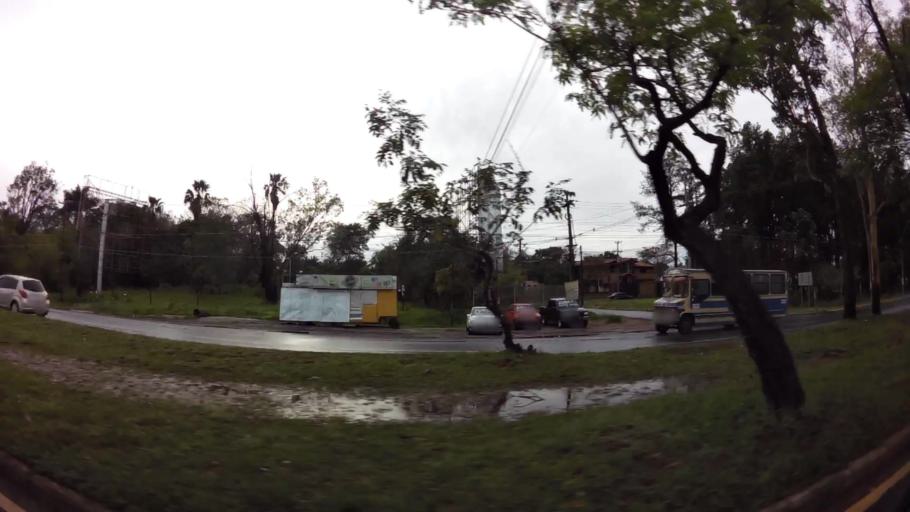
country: PY
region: Central
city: Fernando de la Mora
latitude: -25.2580
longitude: -57.5147
